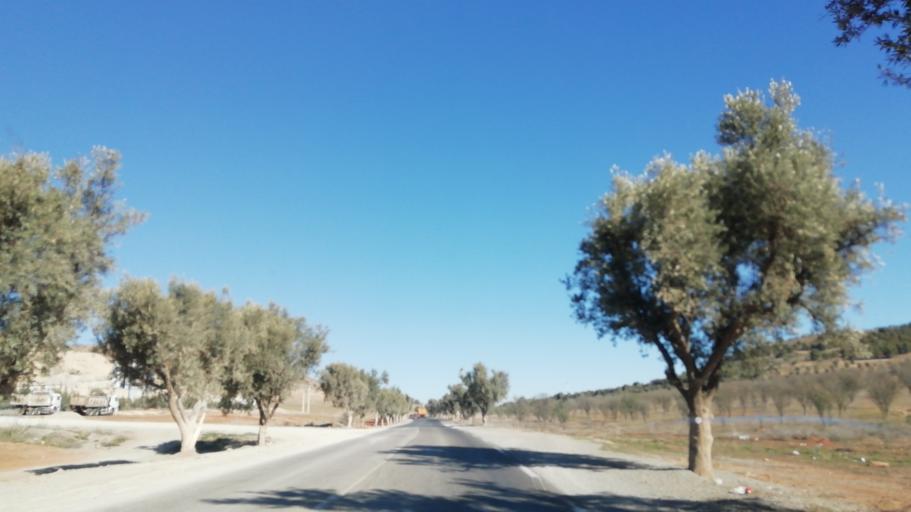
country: DZ
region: Mascara
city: Mascara
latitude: 35.2384
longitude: 0.1175
